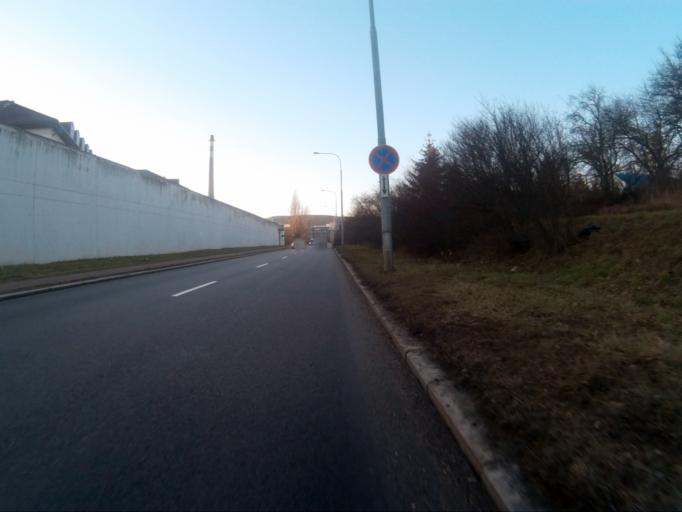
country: CZ
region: South Moravian
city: Moravany
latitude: 49.1758
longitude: 16.5804
